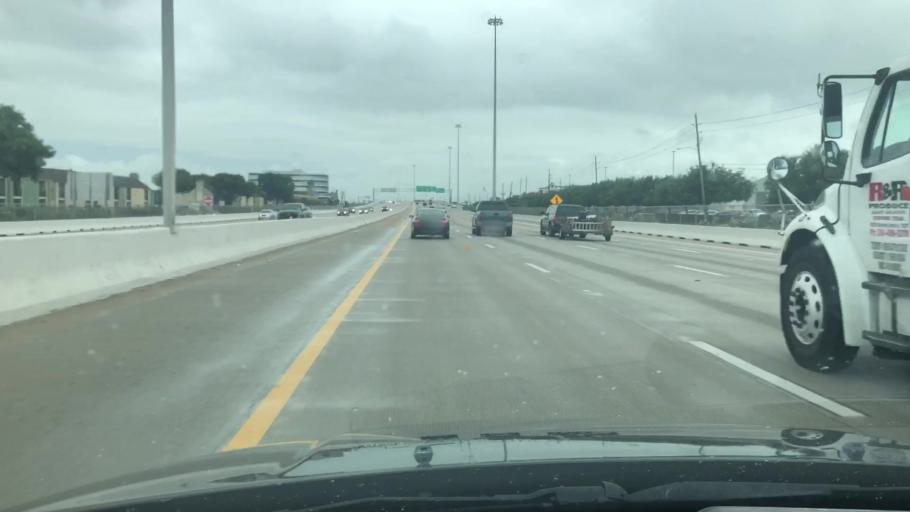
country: US
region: Texas
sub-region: Fort Bend County
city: Meadows Place
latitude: 29.6811
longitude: -95.5591
